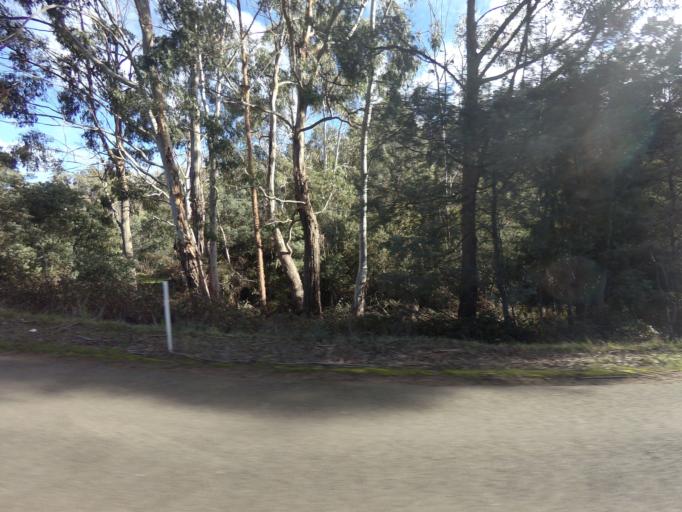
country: AU
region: Tasmania
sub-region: Derwent Valley
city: New Norfolk
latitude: -42.8038
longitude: 147.1375
